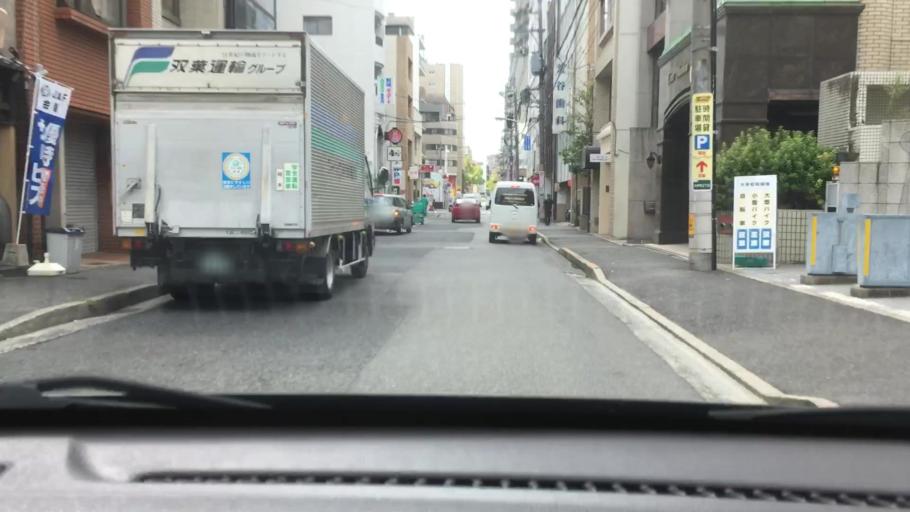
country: JP
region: Hiroshima
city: Hiroshima-shi
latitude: 34.3926
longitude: 132.4554
